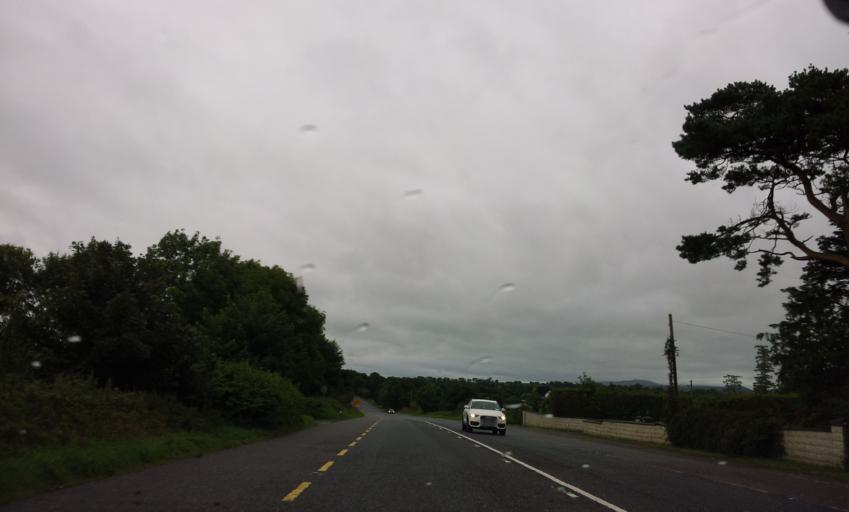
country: IE
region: Munster
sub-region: County Cork
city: Mitchelstown
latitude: 52.2856
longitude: -8.2242
